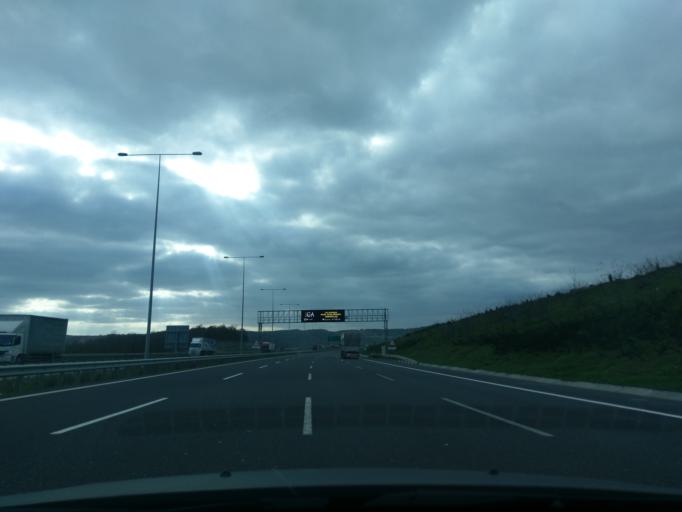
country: TR
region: Istanbul
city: Kemerburgaz
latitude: 41.2220
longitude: 28.8395
